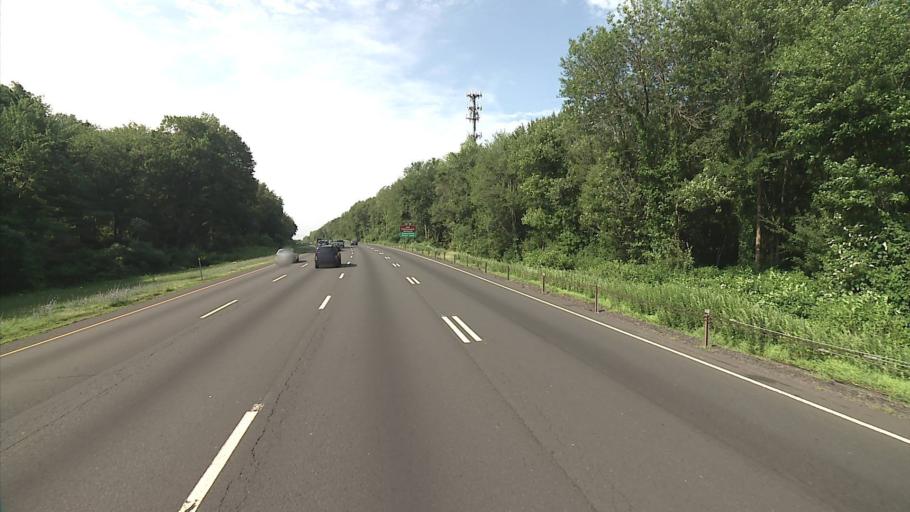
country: US
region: Connecticut
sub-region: New Haven County
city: Meriden
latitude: 41.5582
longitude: -72.7422
